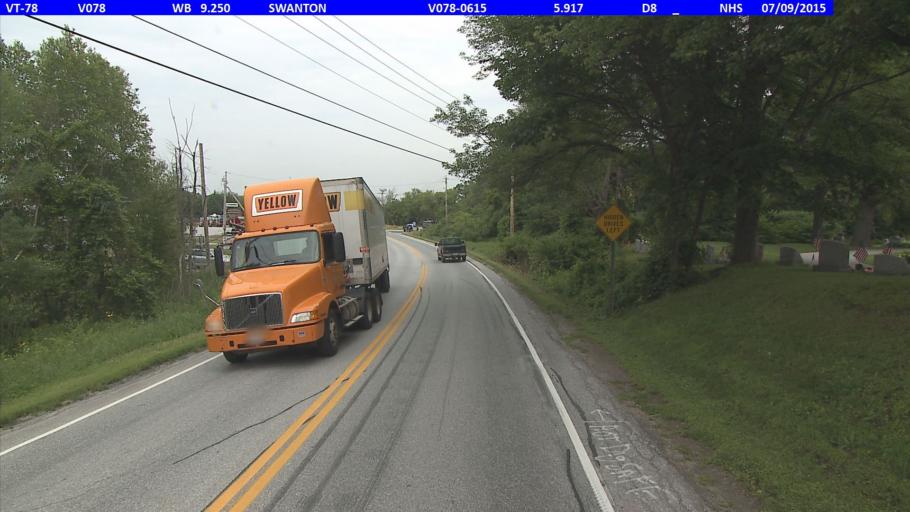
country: US
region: Vermont
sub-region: Franklin County
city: Swanton
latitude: 44.9298
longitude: -73.1271
